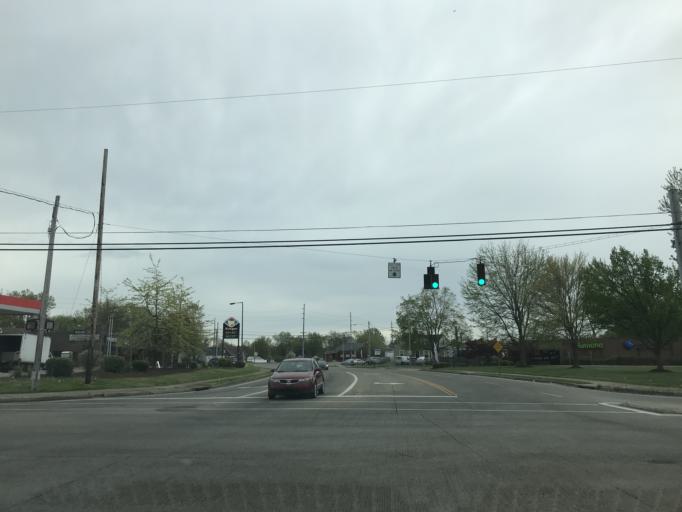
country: US
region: Kentucky
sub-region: Jefferson County
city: West Buechel
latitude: 38.1969
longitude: -85.6633
